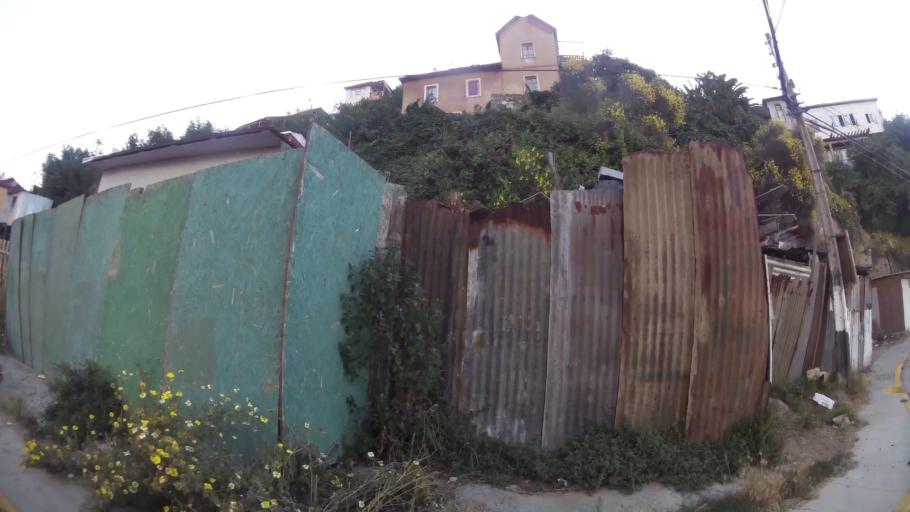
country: CL
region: Valparaiso
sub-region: Provincia de Valparaiso
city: Valparaiso
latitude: -33.0562
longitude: -71.6089
